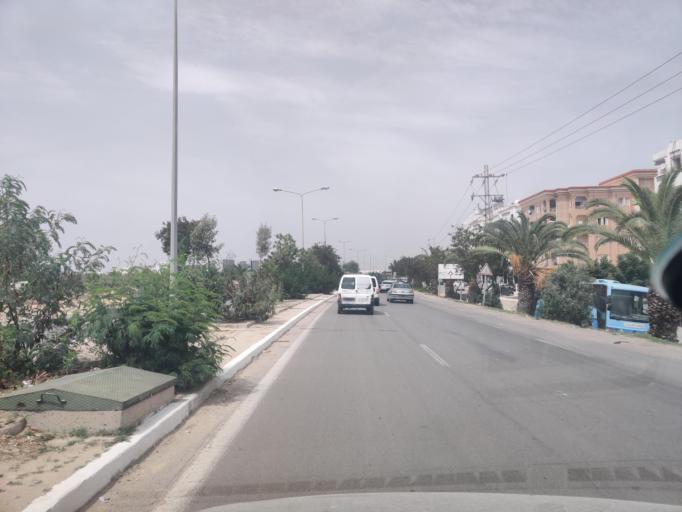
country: TN
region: Susah
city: Hammam Sousse
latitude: 35.8384
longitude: 10.5851
